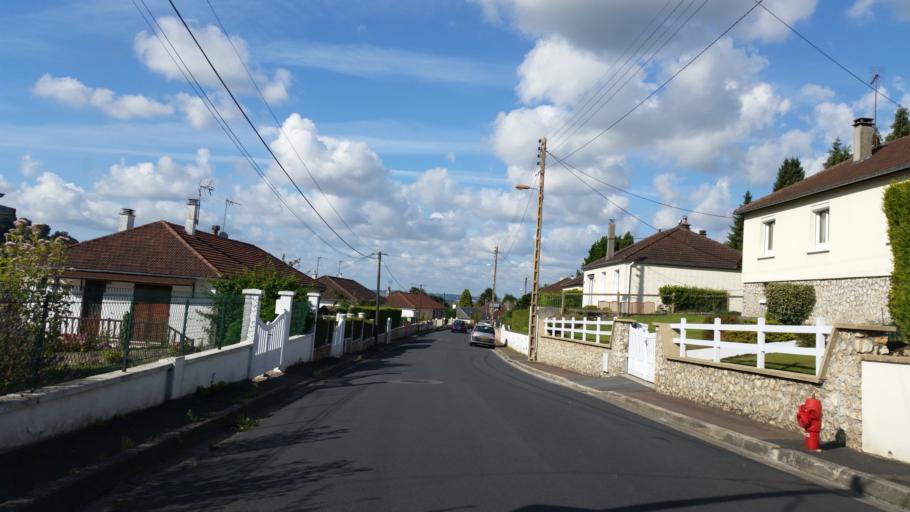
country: FR
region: Lower Normandy
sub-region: Departement du Calvados
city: Honfleur
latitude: 49.4105
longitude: 0.2279
